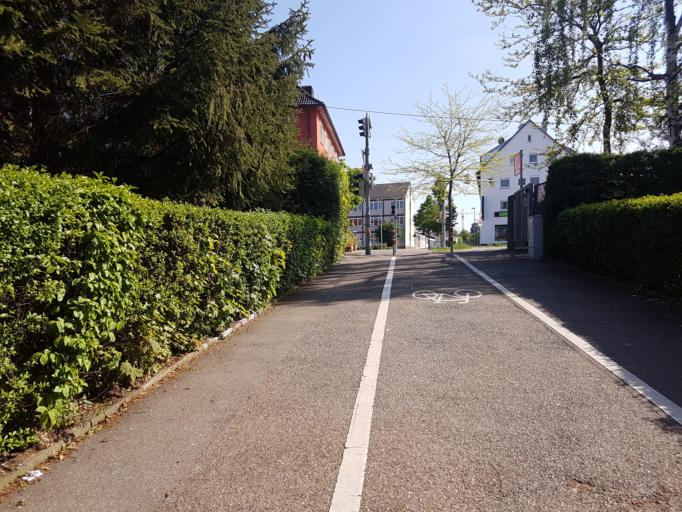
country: DE
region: Baden-Wuerttemberg
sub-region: Regierungsbezirk Stuttgart
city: Ludwigsburg
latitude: 48.8934
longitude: 9.1747
